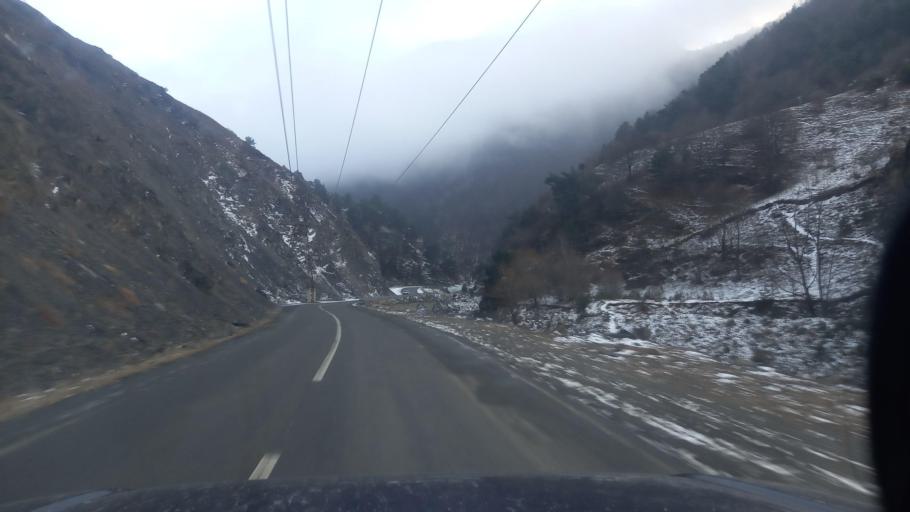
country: RU
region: Ingushetiya
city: Dzhayrakh
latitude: 42.7973
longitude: 44.7616
